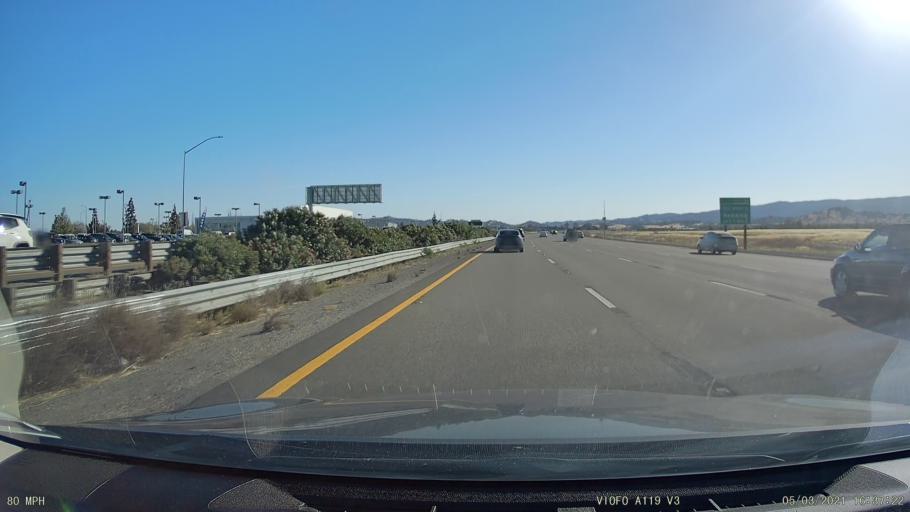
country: US
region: California
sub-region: Solano County
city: Hartley
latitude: 38.3862
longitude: -121.9376
